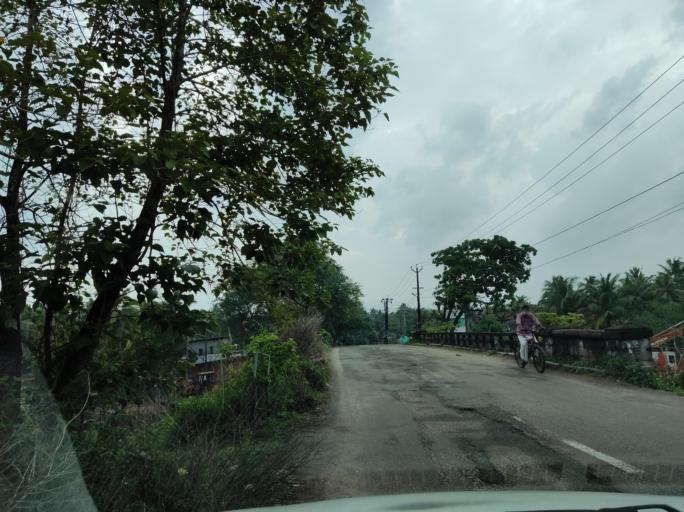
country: IN
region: Kerala
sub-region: Alappuzha
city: Kayankulam
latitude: 9.2587
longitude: 76.4121
